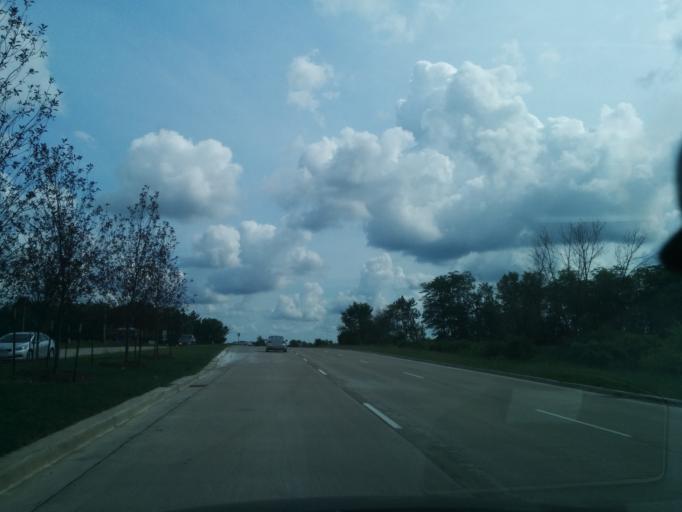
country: US
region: Illinois
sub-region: Cook County
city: Orland Hills
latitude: 41.5737
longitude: -87.8518
